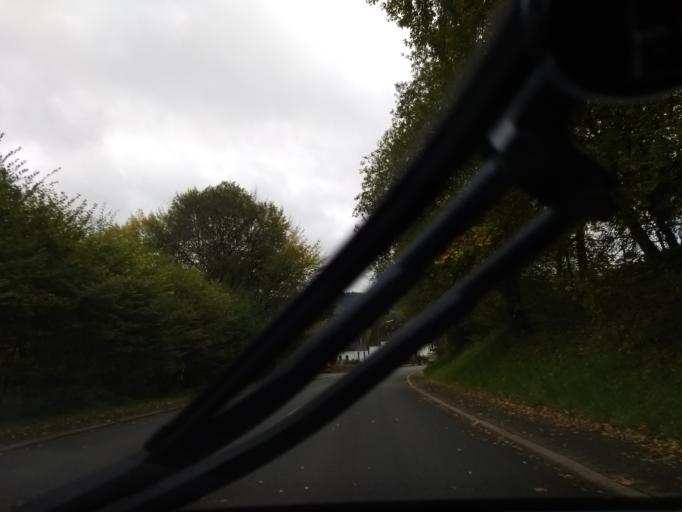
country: DE
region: North Rhine-Westphalia
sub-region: Regierungsbezirk Arnsberg
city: Lennestadt
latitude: 51.1974
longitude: 8.0553
